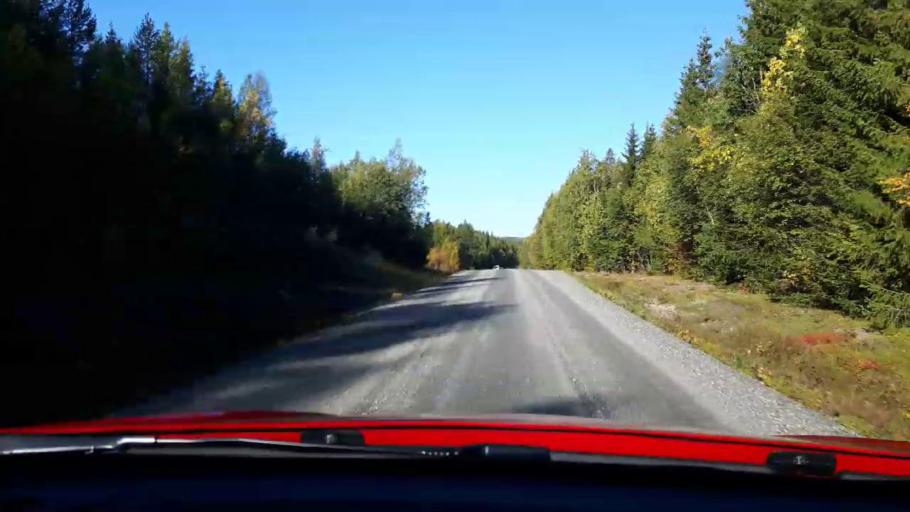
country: NO
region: Nord-Trondelag
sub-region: Lierne
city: Sandvika
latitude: 64.5237
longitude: 14.0728
